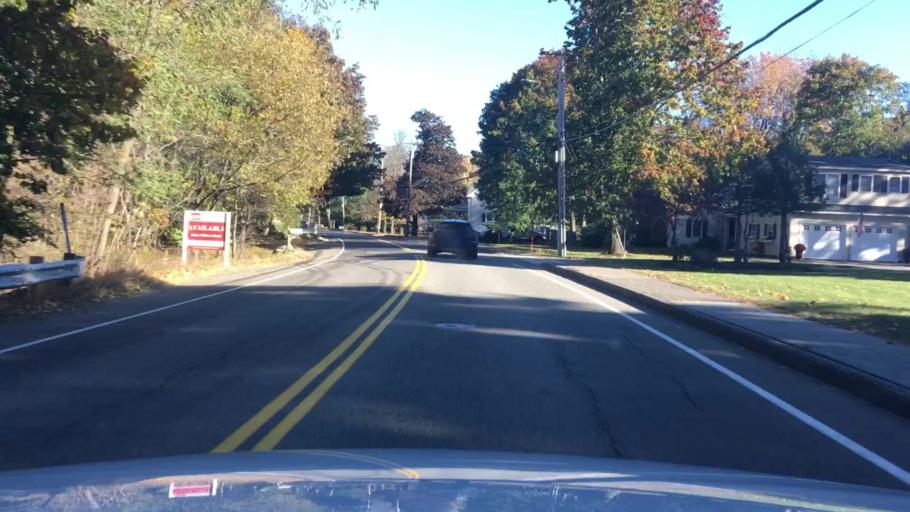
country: US
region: Maine
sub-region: Cumberland County
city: Falmouth
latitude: 43.7235
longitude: -70.2407
